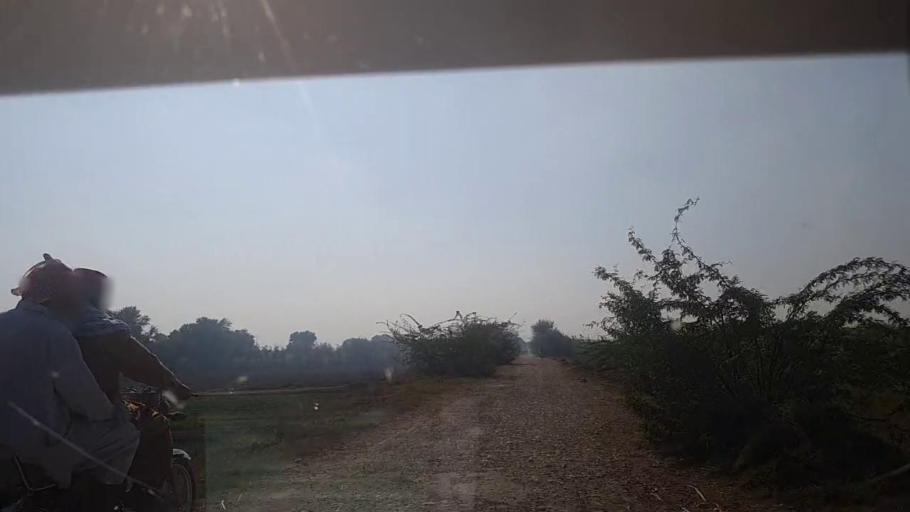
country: PK
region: Sindh
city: Gambat
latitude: 27.3735
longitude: 68.5712
